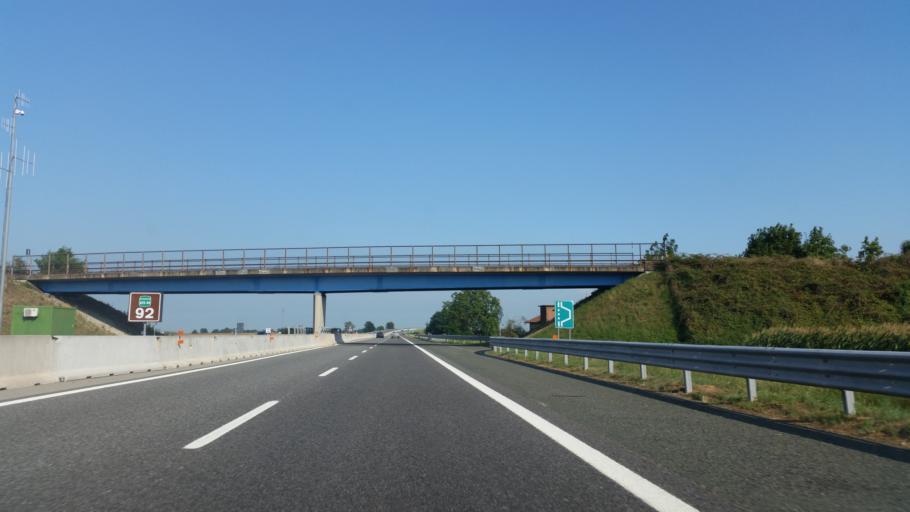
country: IT
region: Piedmont
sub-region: Provincia di Vercelli
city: Tronzano Vercellese
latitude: 45.3484
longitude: 8.1921
